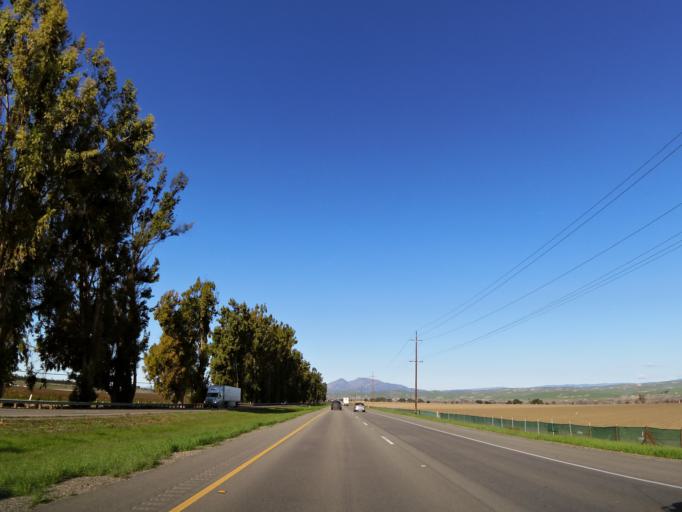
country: US
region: California
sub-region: Monterey County
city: King City
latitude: 36.2407
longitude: -121.1751
